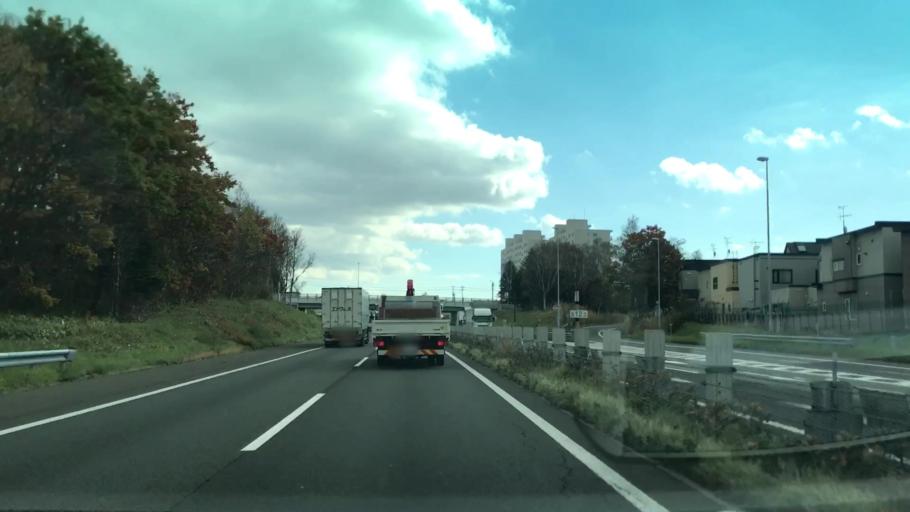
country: JP
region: Hokkaido
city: Kitahiroshima
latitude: 42.9782
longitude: 141.4769
